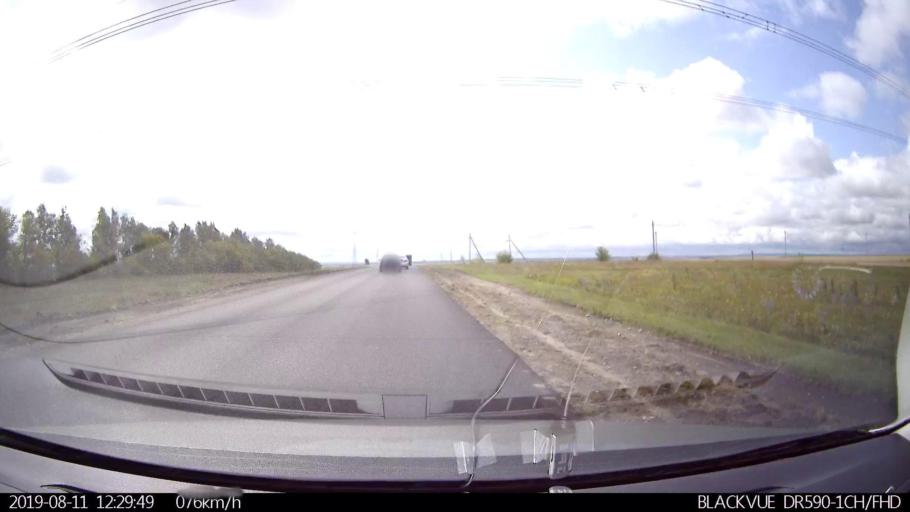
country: RU
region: Ulyanovsk
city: Ignatovka
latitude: 53.8311
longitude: 47.8992
